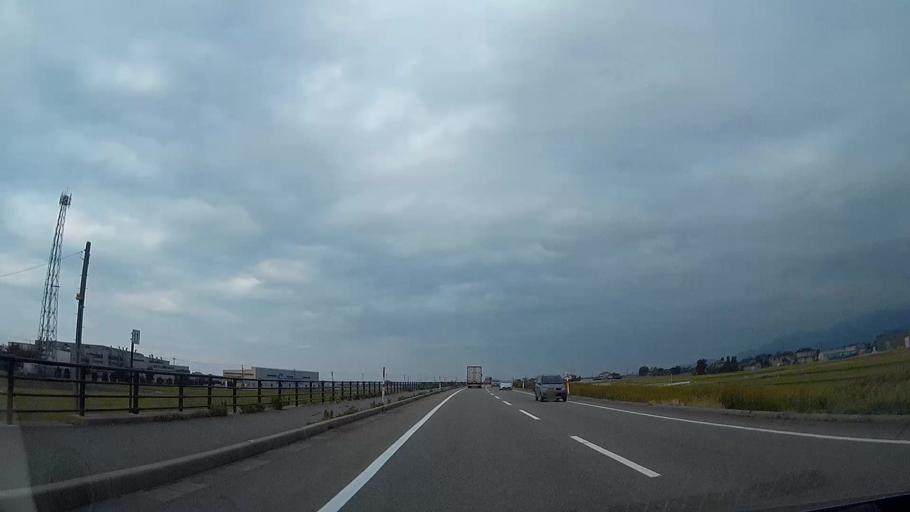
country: JP
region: Toyama
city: Nyuzen
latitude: 36.9230
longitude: 137.4694
